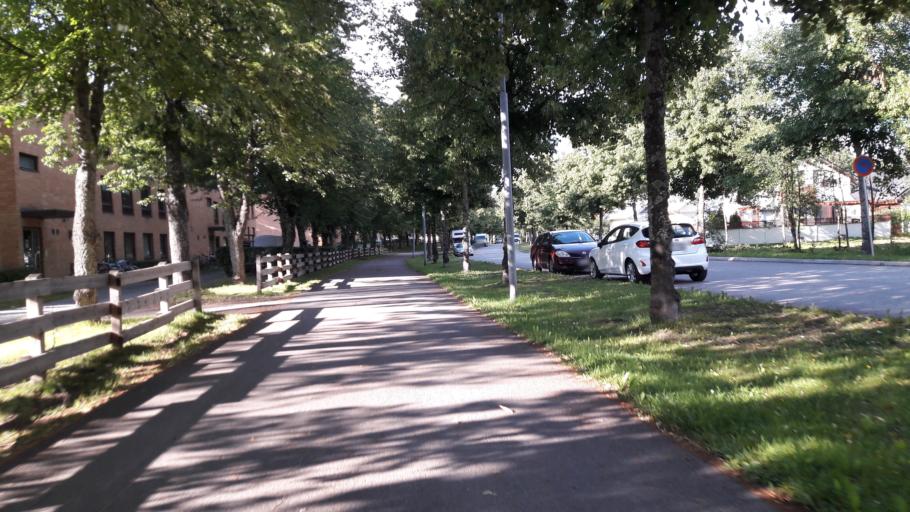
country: FI
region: North Karelia
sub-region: Joensuu
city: Joensuu
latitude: 62.6047
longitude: 29.8043
